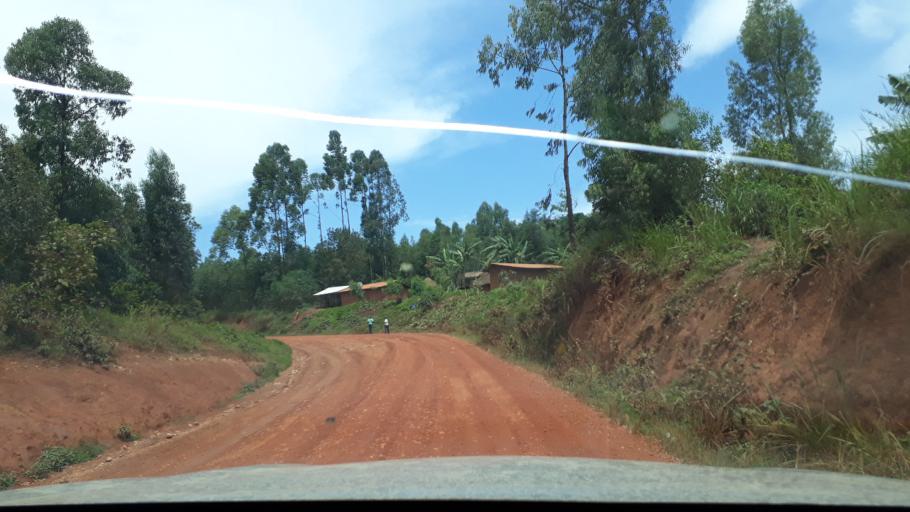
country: CD
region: Eastern Province
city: Bunia
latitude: 1.7272
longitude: 30.3186
